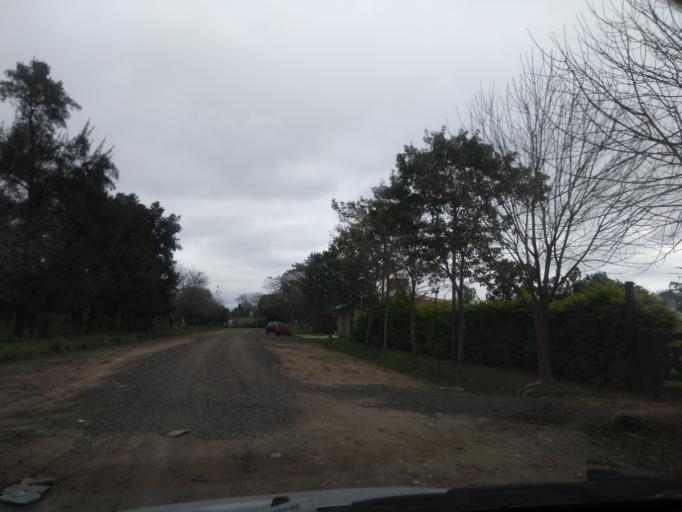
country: AR
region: Chaco
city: Barranqueras
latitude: -27.4248
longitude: -58.9337
